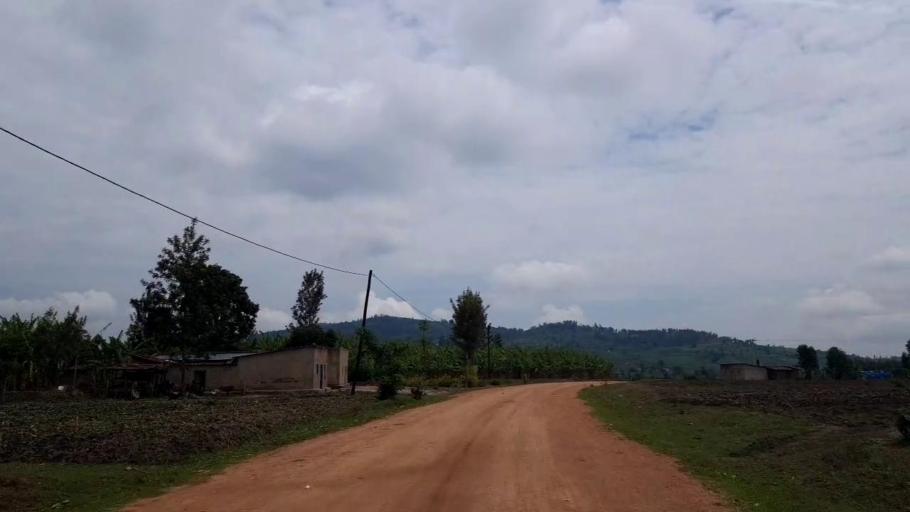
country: RW
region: Northern Province
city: Byumba
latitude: -1.4985
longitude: 30.2076
